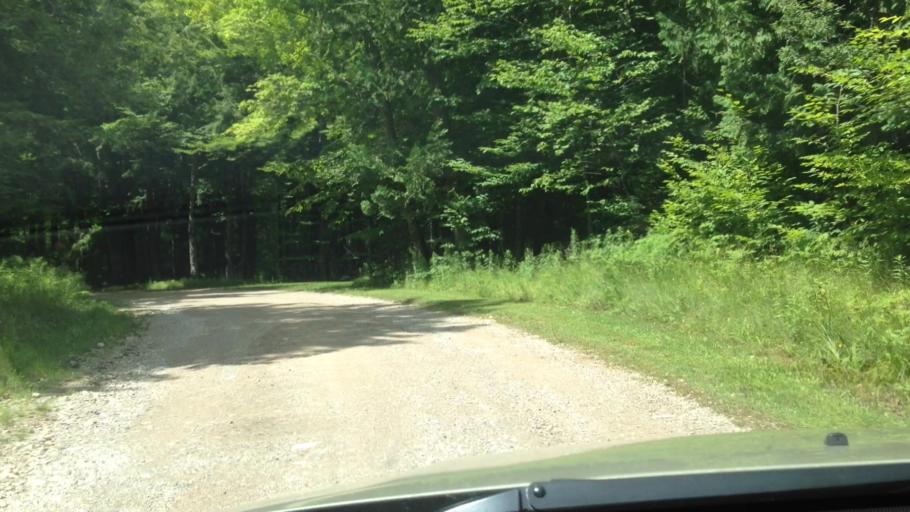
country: US
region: Michigan
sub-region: Menominee County
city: Menominee
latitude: 45.4000
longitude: -87.3618
